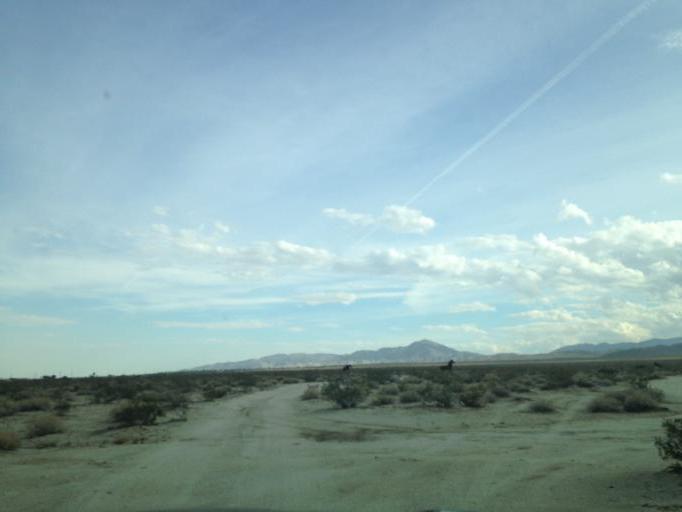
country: US
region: California
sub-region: San Diego County
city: Borrego Springs
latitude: 33.2109
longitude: -116.3551
